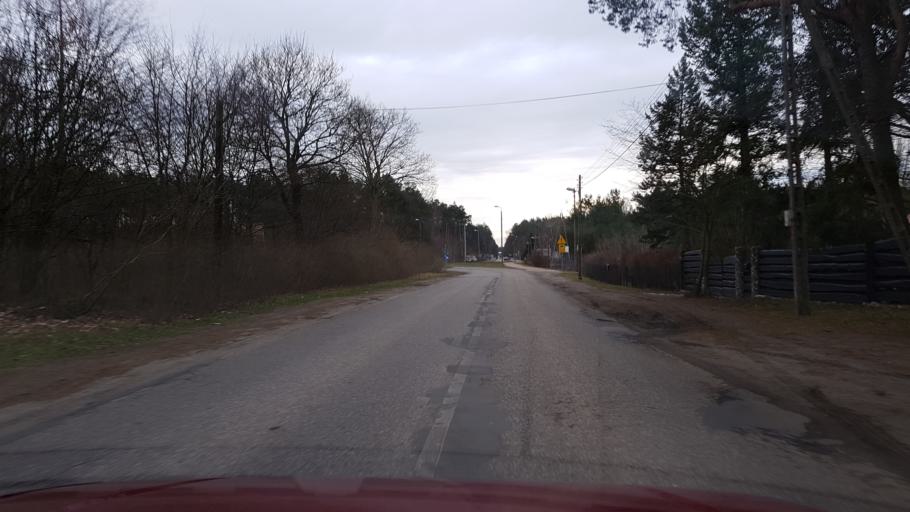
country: PL
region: West Pomeranian Voivodeship
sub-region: Powiat policki
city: Dobra
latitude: 53.5350
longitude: 14.4673
